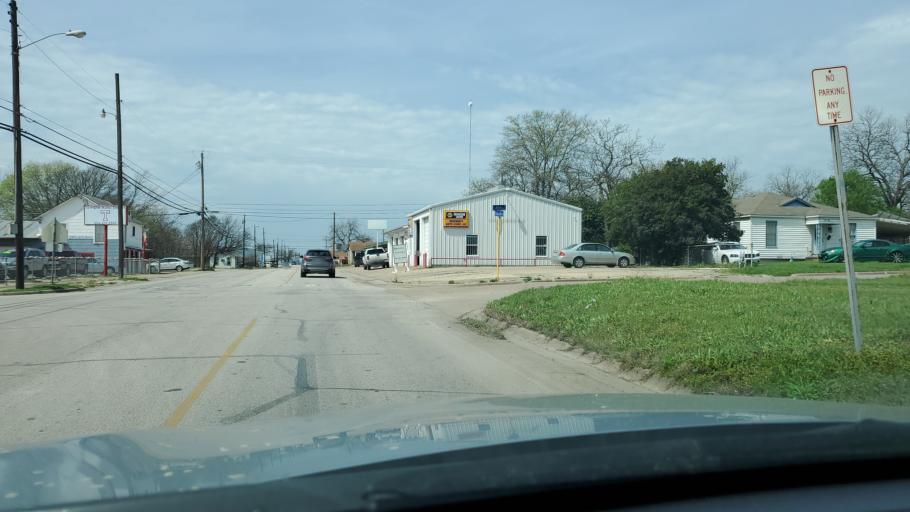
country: US
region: Texas
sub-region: Bell County
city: Temple
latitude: 31.0907
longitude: -97.3696
